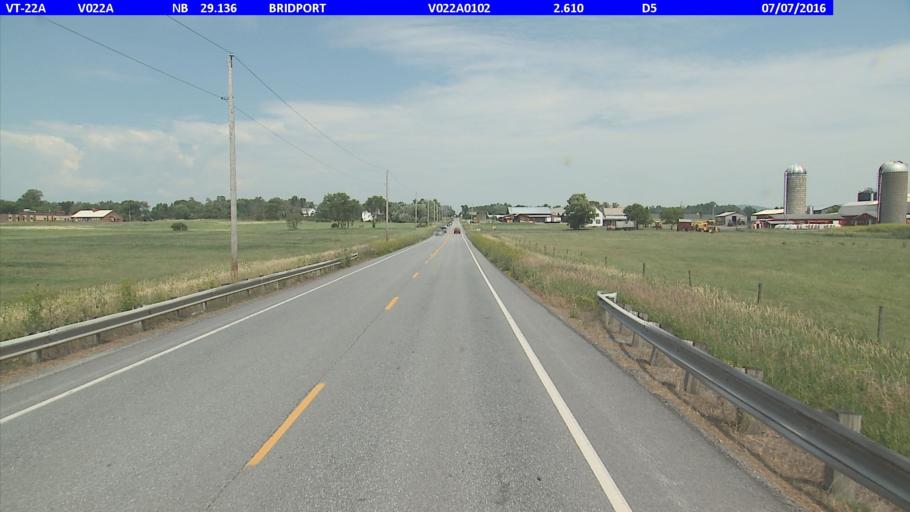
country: US
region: Vermont
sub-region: Addison County
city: Middlebury (village)
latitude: 43.9779
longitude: -73.3119
